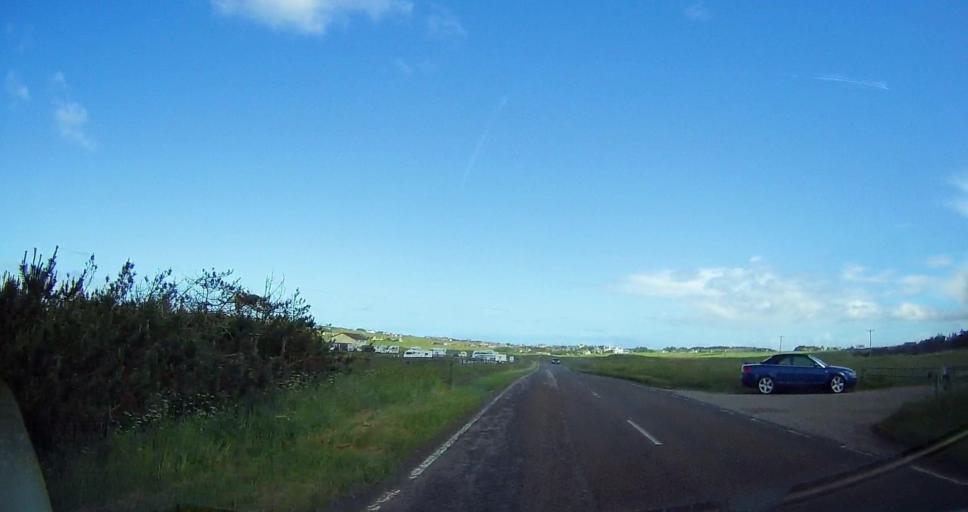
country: GB
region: Scotland
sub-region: Highland
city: Thurso
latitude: 58.6130
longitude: -3.3435
